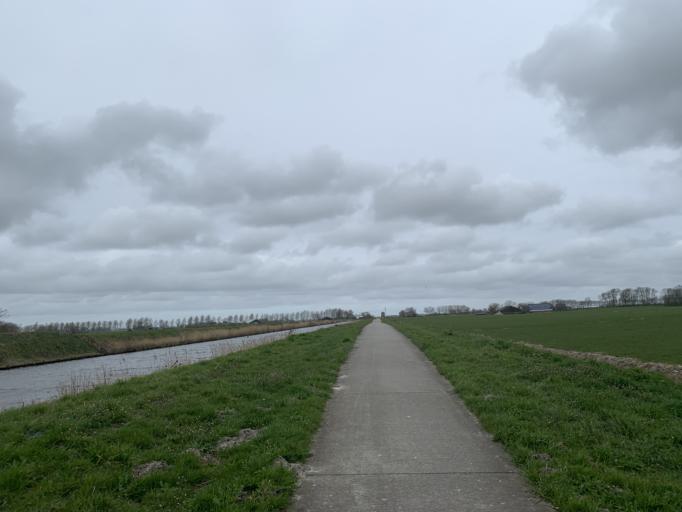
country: NL
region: Groningen
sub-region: Gemeente Zuidhorn
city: Aduard
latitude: 53.2620
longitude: 6.5079
